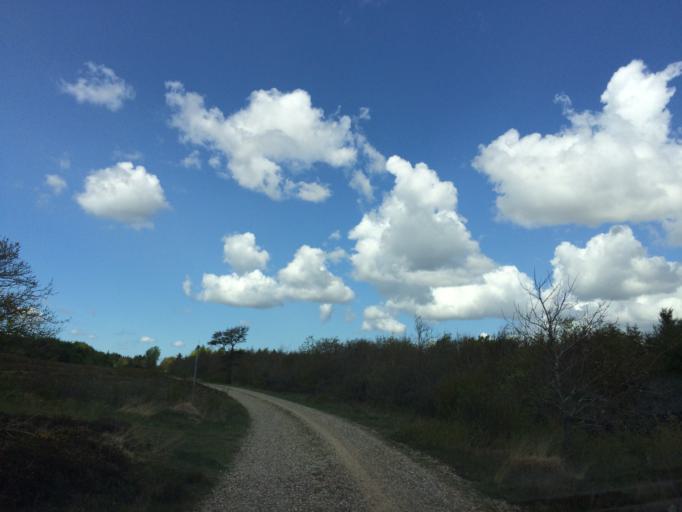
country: DK
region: Central Jutland
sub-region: Holstebro Kommune
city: Ulfborg
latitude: 56.2843
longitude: 8.4627
